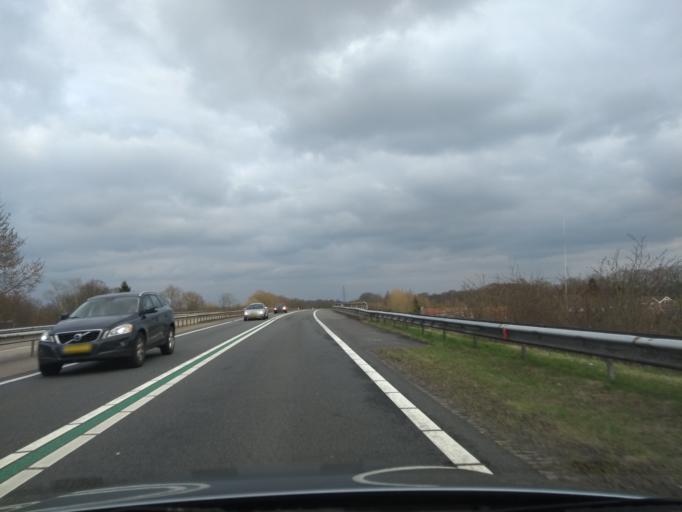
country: NL
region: Overijssel
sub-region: Gemeente Staphorst
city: Staphorst
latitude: 52.5888
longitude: 6.2238
